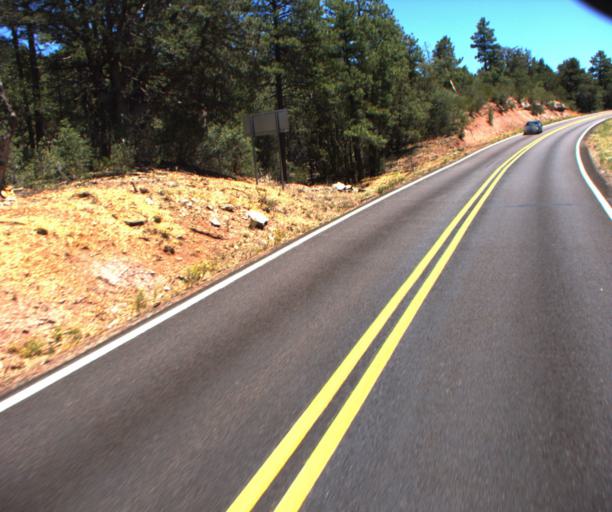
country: US
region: Arizona
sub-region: Gila County
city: Pine
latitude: 34.3629
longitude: -111.4272
